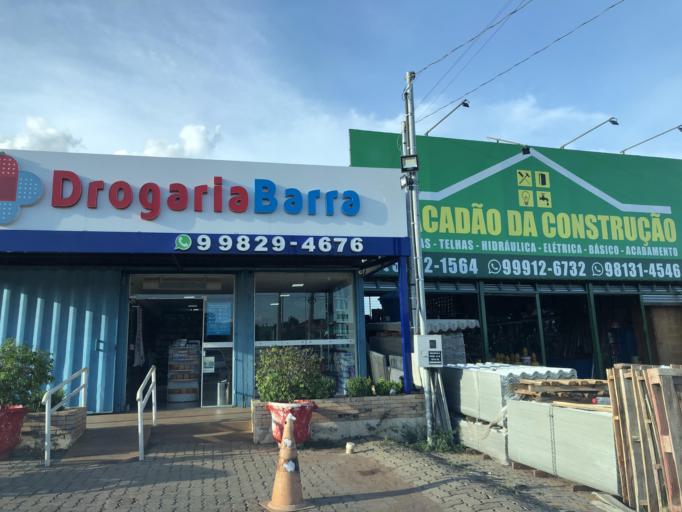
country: BR
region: Federal District
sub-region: Brasilia
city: Brasilia
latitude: -15.8156
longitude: -47.7869
